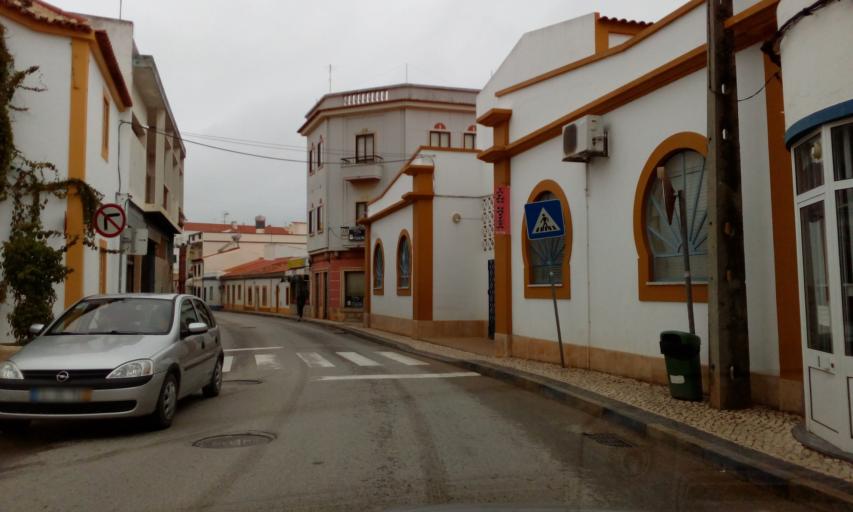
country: PT
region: Faro
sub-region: Albufeira
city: Guia
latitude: 37.1637
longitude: -8.3026
